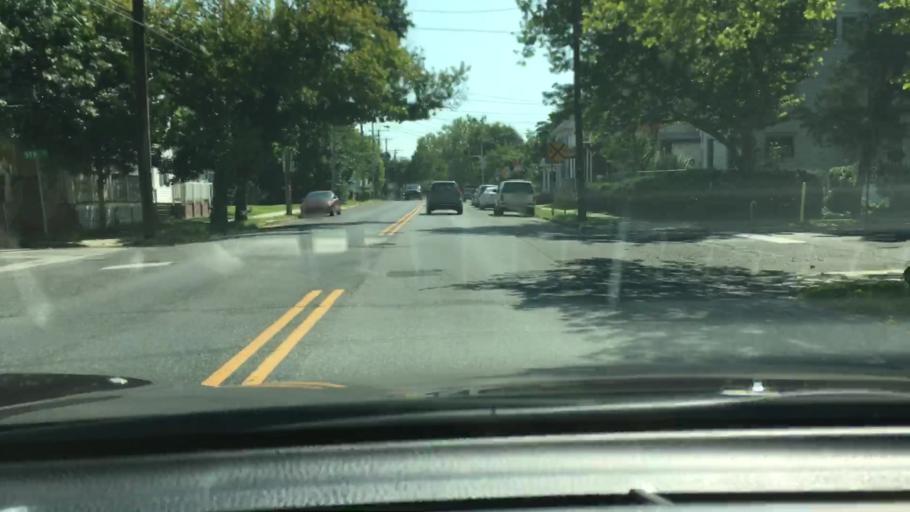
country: US
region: New Jersey
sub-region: Cumberland County
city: Millville
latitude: 39.3954
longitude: -75.0332
